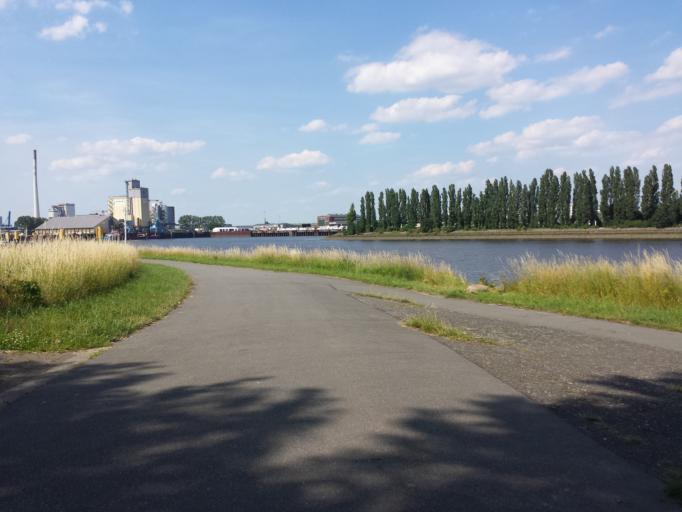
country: DE
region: Bremen
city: Bremen
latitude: 53.1081
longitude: 8.7415
